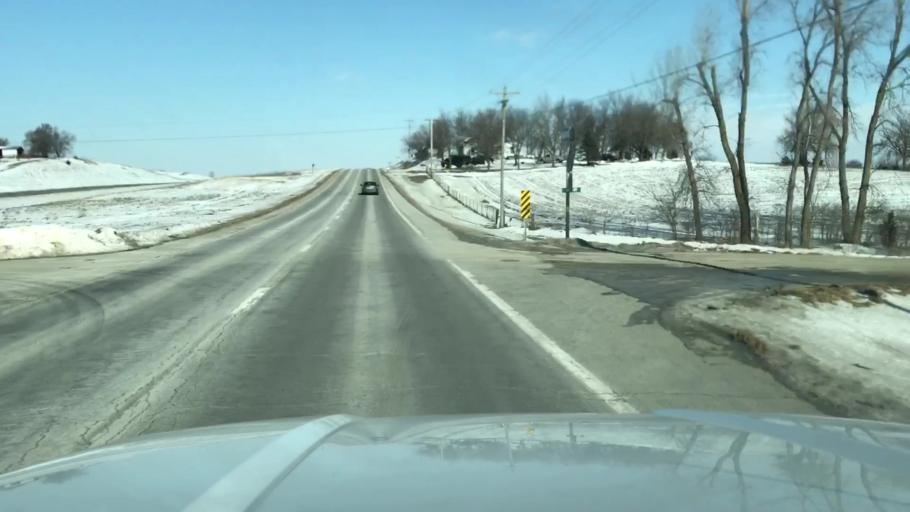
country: US
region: Missouri
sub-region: Andrew County
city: Savannah
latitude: 40.0105
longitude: -94.8796
